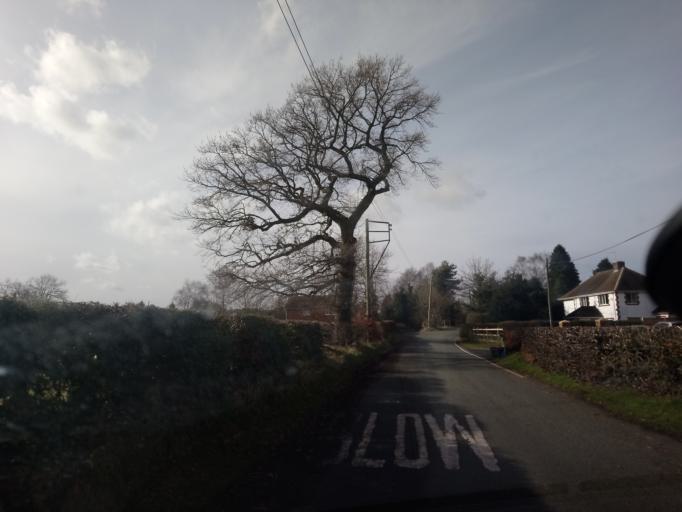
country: GB
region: England
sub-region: Shropshire
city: Stoke upon Tern
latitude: 52.8490
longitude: -2.5618
